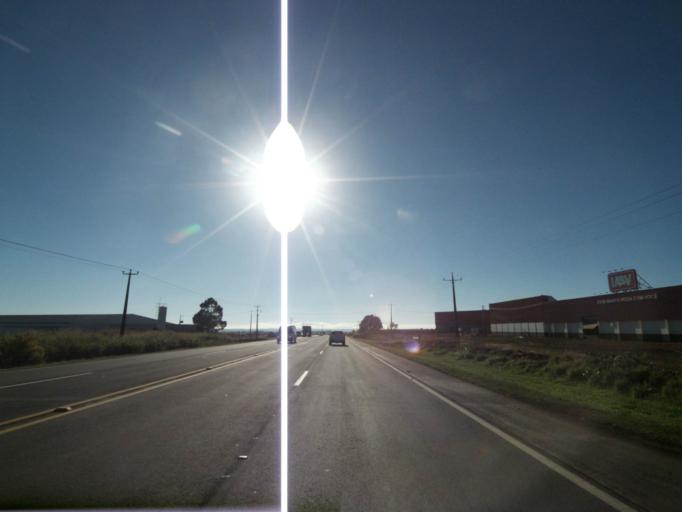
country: BR
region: Parana
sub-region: Mandaguari
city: Mandaguari
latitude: -23.5053
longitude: -51.6968
